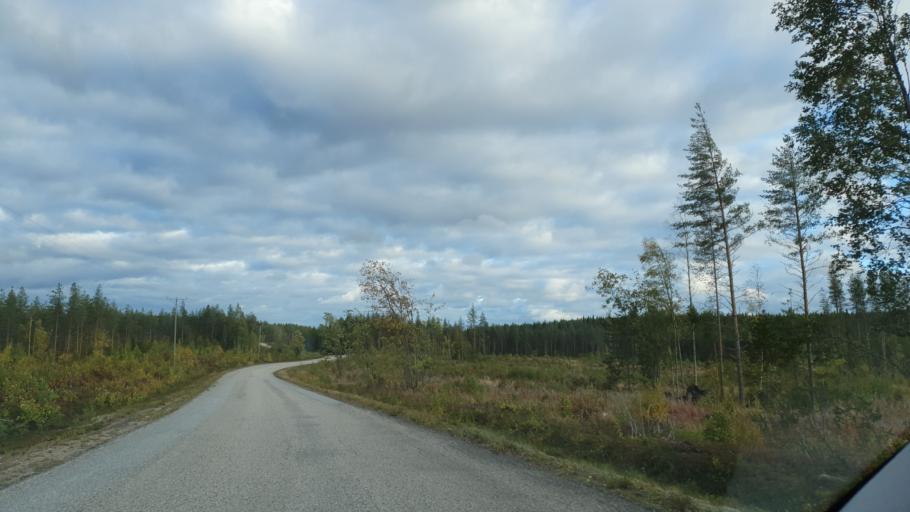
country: FI
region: North Karelia
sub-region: Pielisen Karjala
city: Lieksa
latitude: 63.9170
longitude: 30.1701
